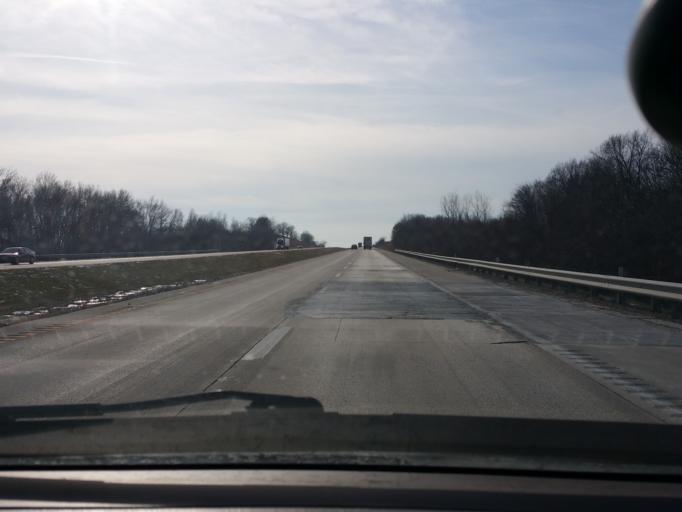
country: US
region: Missouri
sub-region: Clay County
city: Kearney
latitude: 39.4115
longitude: -94.3489
